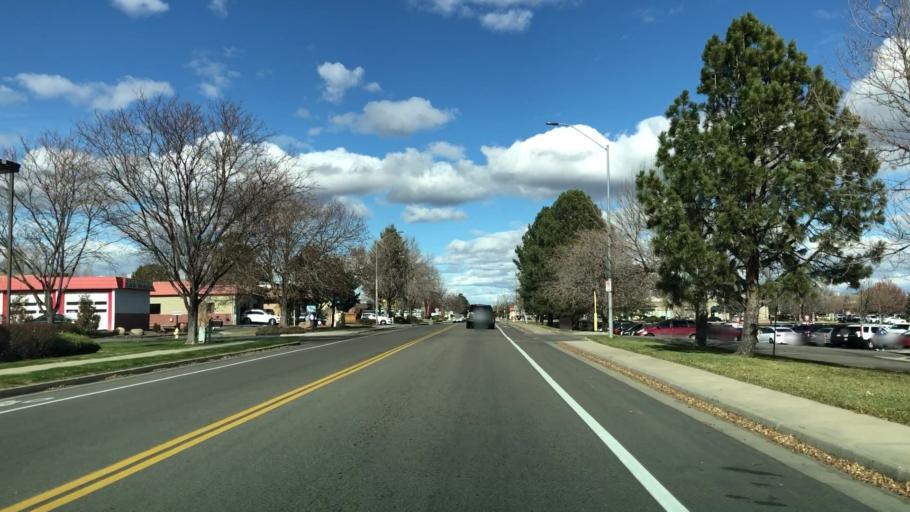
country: US
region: Colorado
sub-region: Larimer County
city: Fort Collins
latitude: 40.5269
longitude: -105.0795
